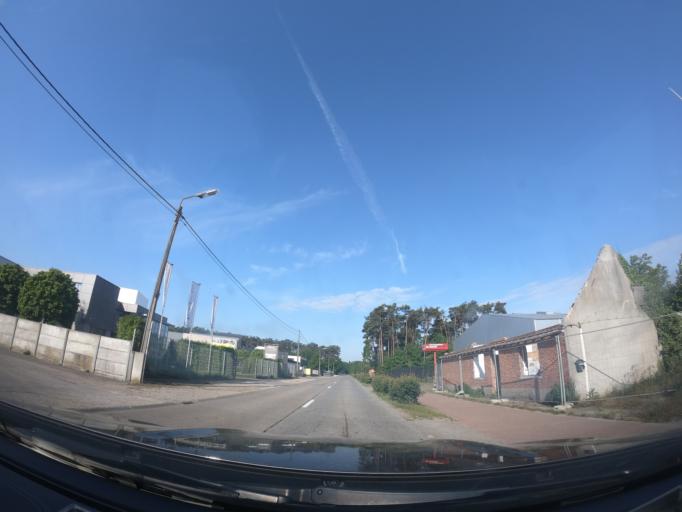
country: BE
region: Flanders
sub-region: Provincie Antwerpen
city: Olen
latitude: 51.1494
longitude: 4.8876
